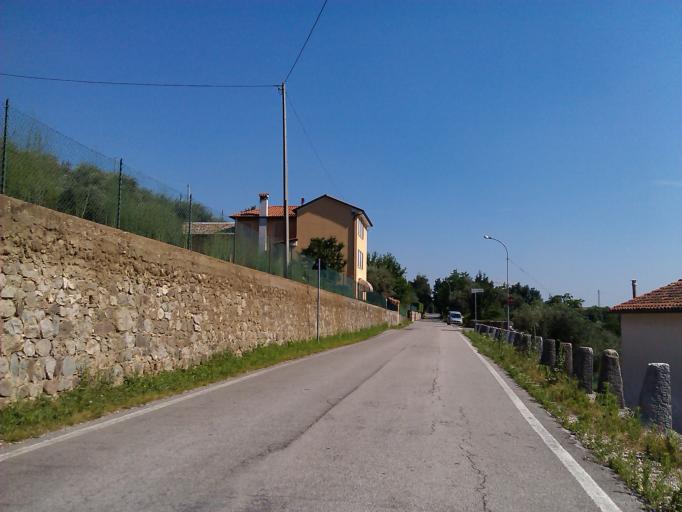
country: IT
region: Veneto
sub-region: Provincia di Vicenza
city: Pove del Grappa
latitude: 45.7984
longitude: 11.7248
